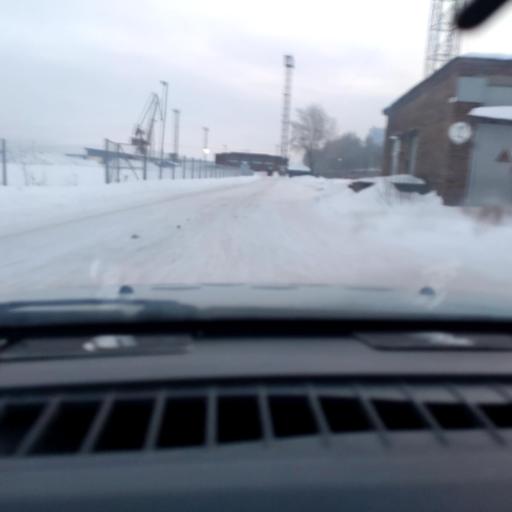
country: RU
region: Perm
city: Perm
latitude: 58.0139
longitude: 56.2023
